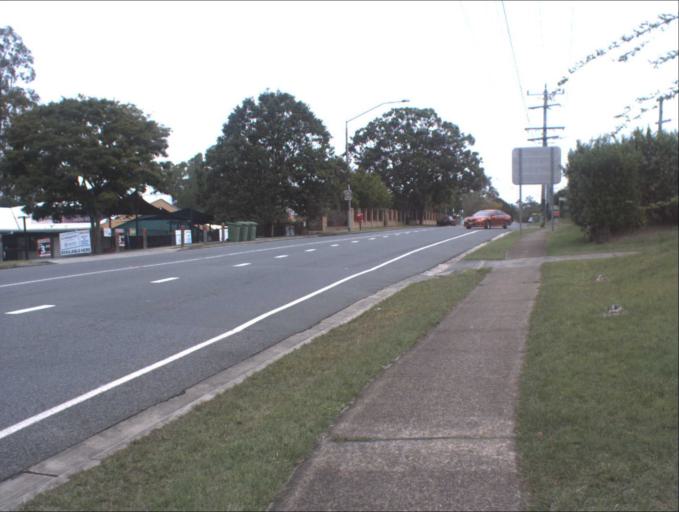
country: AU
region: Queensland
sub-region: Logan
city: Park Ridge South
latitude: -27.6870
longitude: 153.0313
